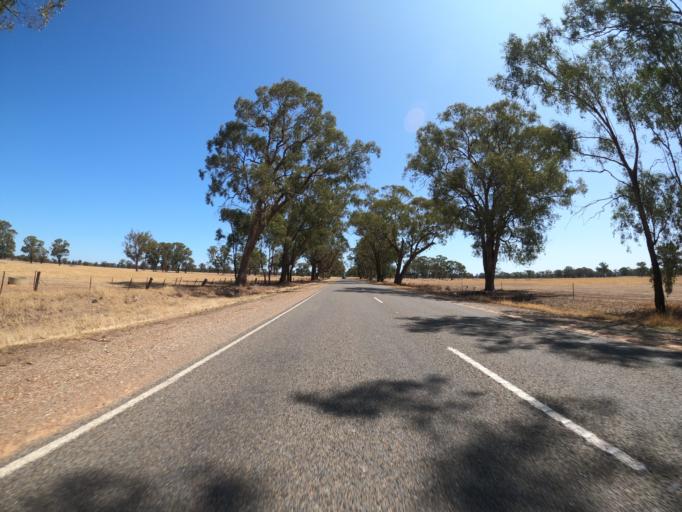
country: AU
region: New South Wales
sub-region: Corowa Shire
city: Corowa
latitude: -36.0705
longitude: 146.3560
